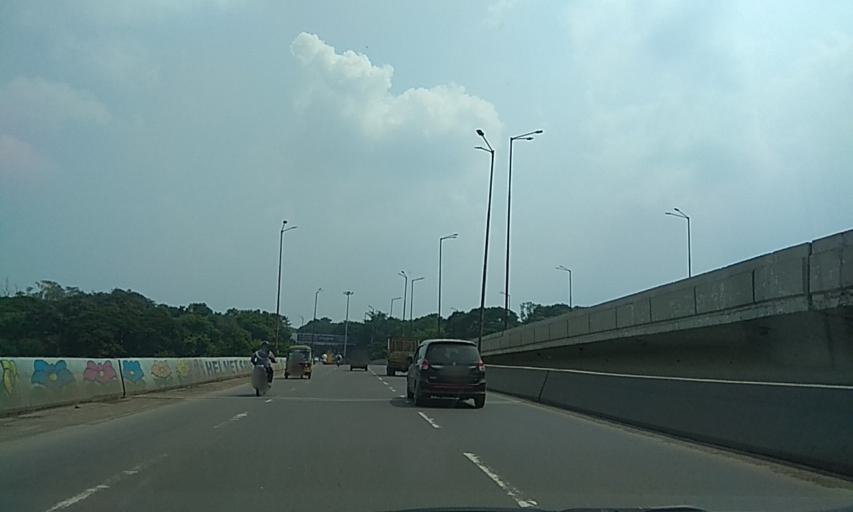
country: IN
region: Maharashtra
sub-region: Pune Division
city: Khadki
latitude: 18.5544
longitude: 73.8627
